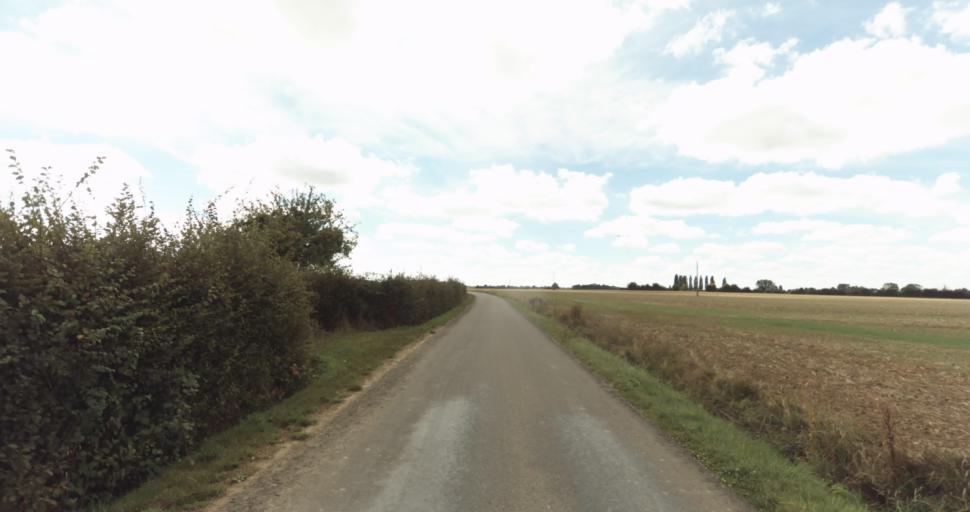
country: FR
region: Lower Normandy
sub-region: Departement du Calvados
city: Orbec
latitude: 48.9171
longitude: 0.3735
